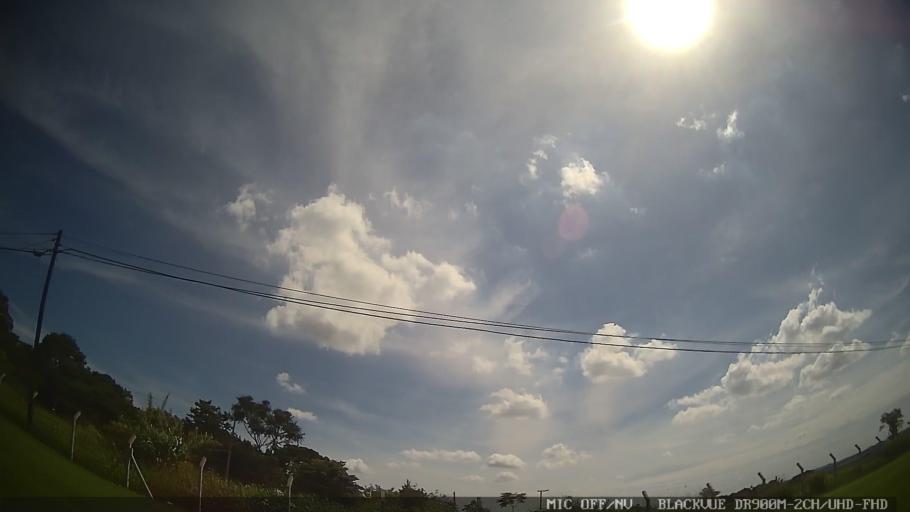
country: BR
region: Sao Paulo
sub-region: Artur Nogueira
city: Artur Nogueira
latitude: -22.6162
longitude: -47.0779
